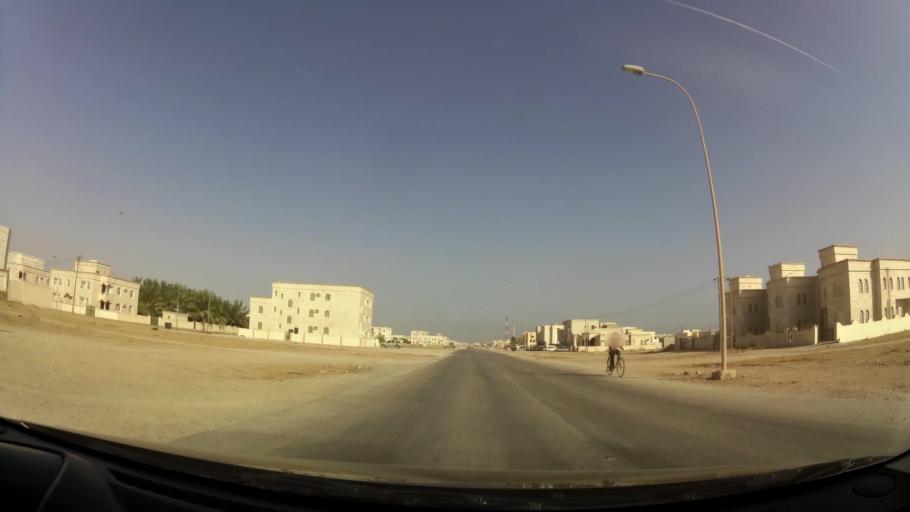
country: OM
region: Zufar
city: Salalah
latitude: 17.0216
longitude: 54.0169
